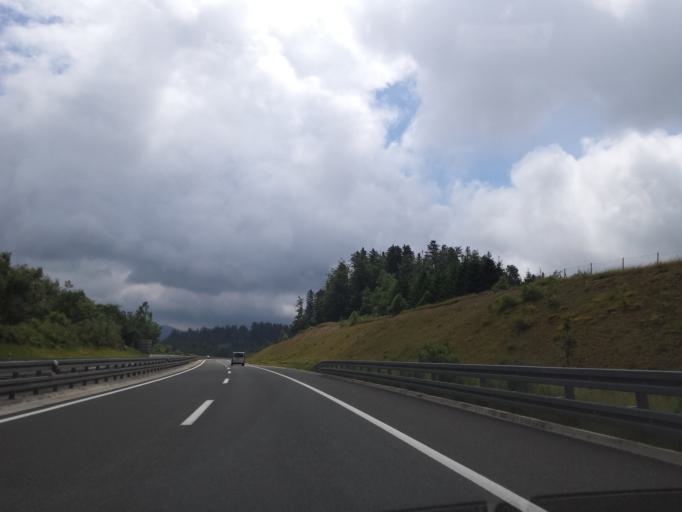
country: HR
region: Primorsko-Goranska
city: Hreljin
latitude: 45.3197
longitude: 14.6681
